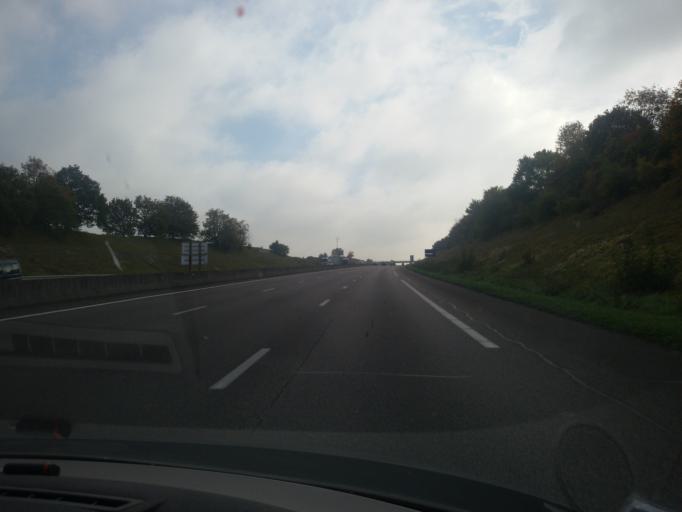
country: FR
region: Haute-Normandie
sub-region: Departement de l'Eure
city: Saint-Pierre-du-Vauvray
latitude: 49.2319
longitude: 1.2048
